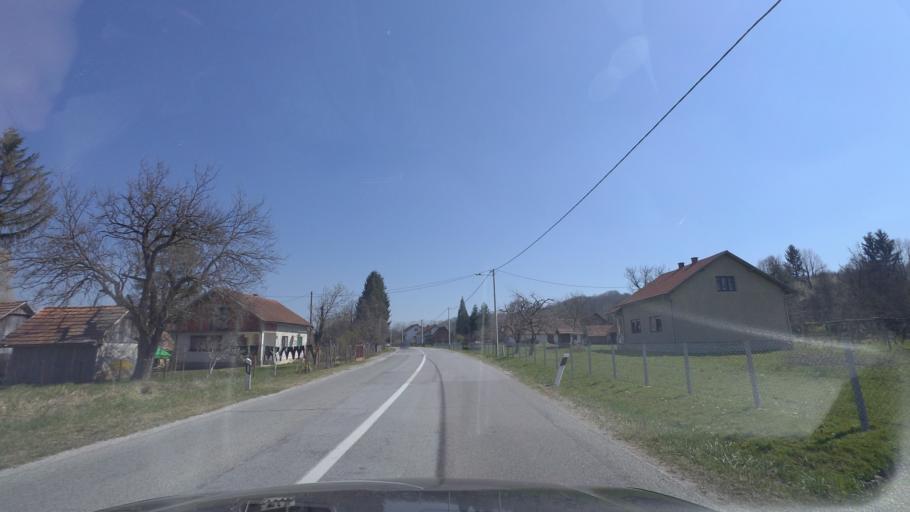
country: HR
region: Sisacko-Moslavacka
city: Gvozd
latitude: 45.3478
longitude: 15.8693
